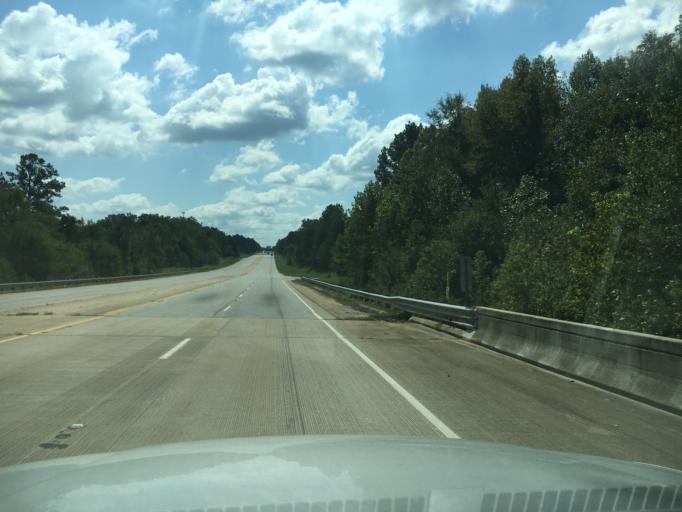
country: US
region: South Carolina
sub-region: Greenwood County
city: Ware Shoals
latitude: 34.3917
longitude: -82.2237
